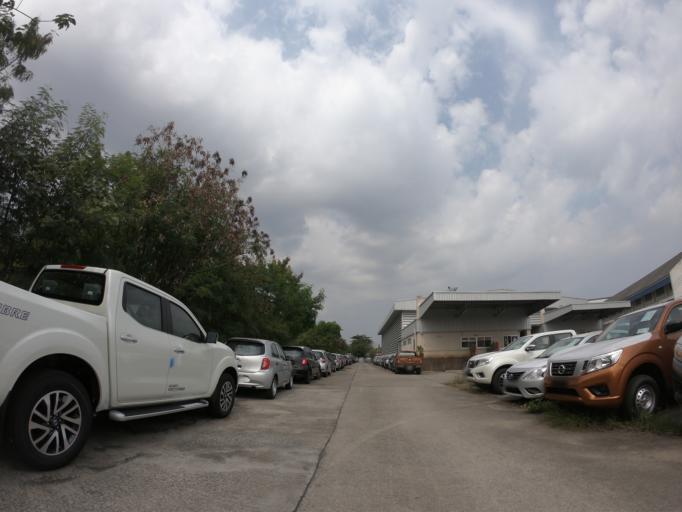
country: TH
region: Chiang Mai
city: Chiang Mai
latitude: 18.7694
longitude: 98.9815
